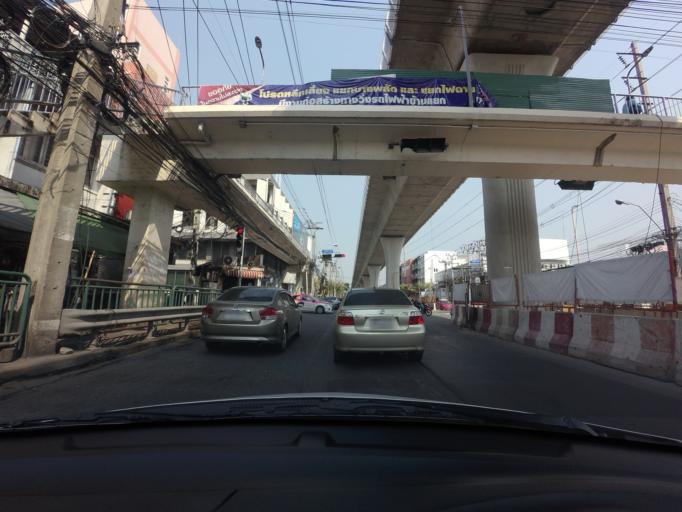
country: TH
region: Bangkok
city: Bangkok Yai
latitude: 13.7412
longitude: 100.4705
